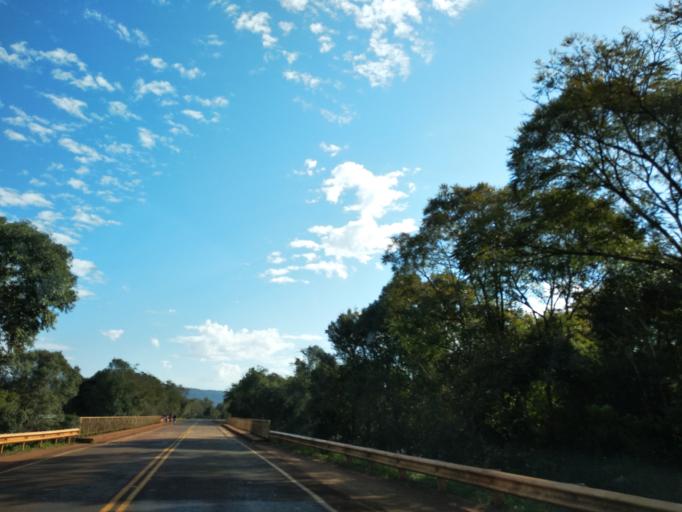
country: AR
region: Misiones
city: Aristobulo del Valle
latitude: -27.1020
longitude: -54.9636
